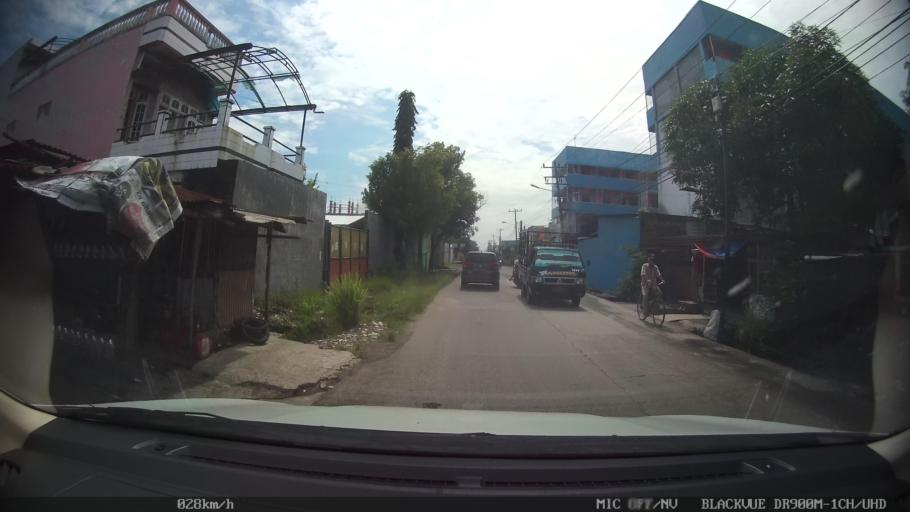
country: ID
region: North Sumatra
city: Medan
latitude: 3.5871
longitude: 98.7151
